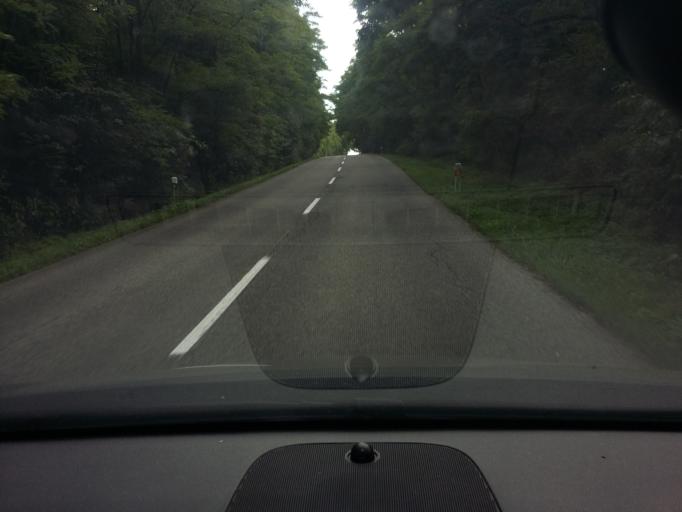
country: SK
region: Trnavsky
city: Gbely
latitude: 48.6858
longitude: 17.1551
